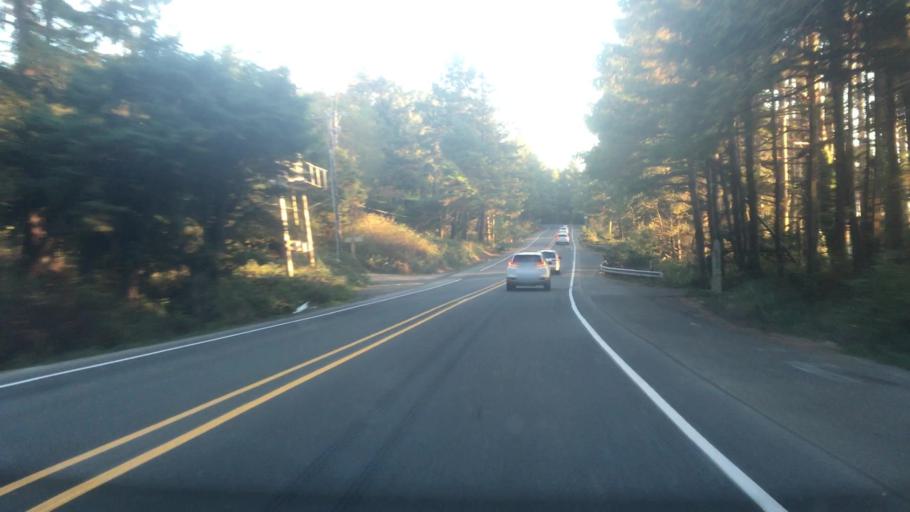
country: US
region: Oregon
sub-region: Clatsop County
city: Cannon Beach
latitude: 45.8454
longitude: -123.9595
